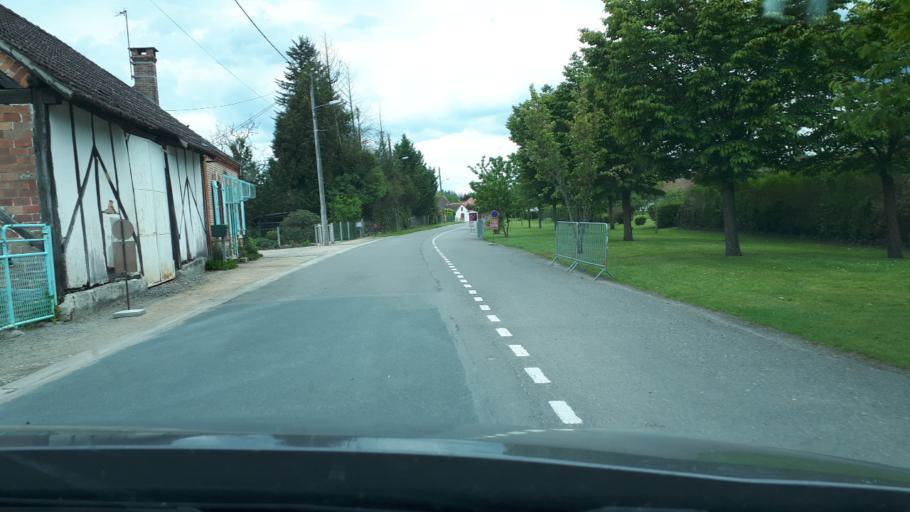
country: FR
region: Centre
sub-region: Departement du Loir-et-Cher
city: Souesmes
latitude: 47.5130
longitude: 2.1496
